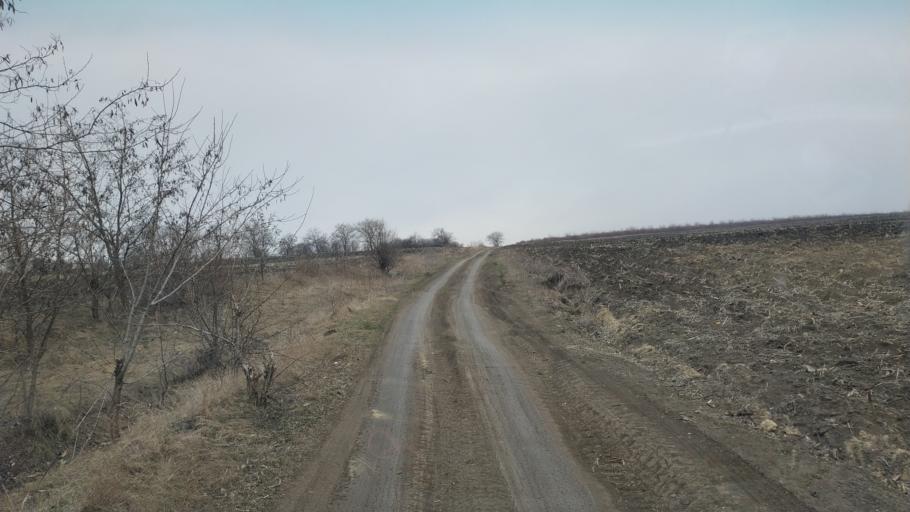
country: MD
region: Chisinau
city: Singera
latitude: 46.8276
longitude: 29.0067
